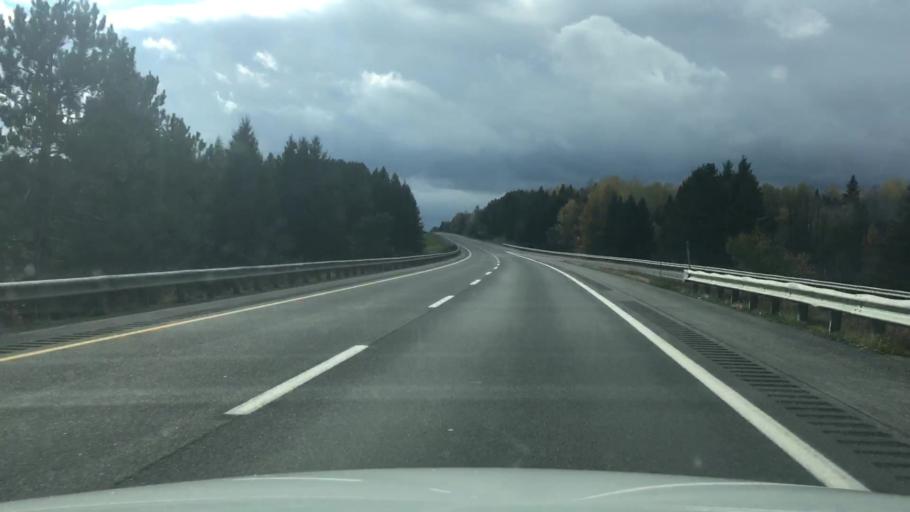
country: US
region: Maine
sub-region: Aroostook County
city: Hodgdon
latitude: 46.1098
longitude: -68.1633
